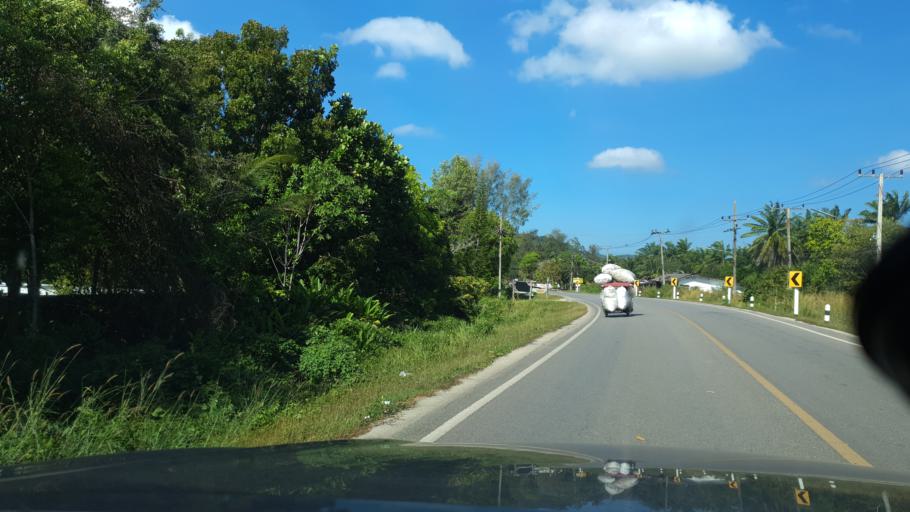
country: TH
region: Krabi
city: Krabi
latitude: 8.0288
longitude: 98.8698
